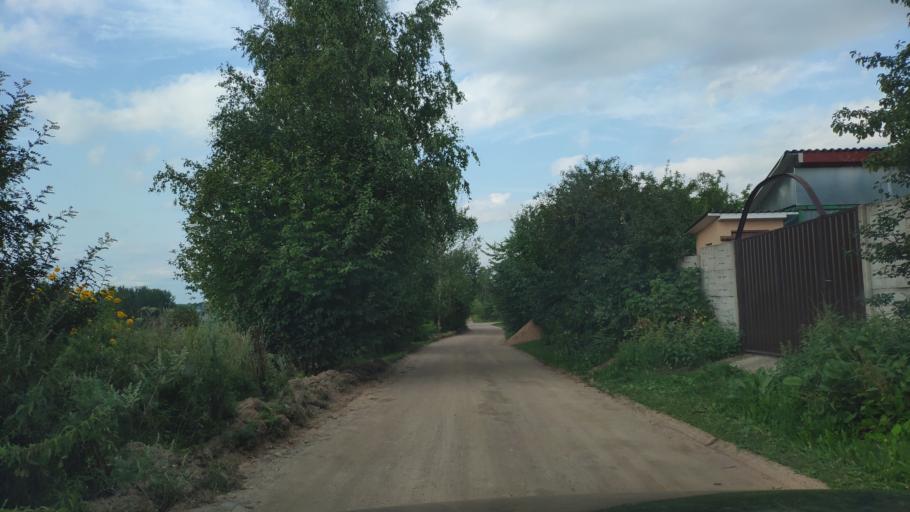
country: BY
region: Minsk
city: Khatsyezhyna
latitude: 53.8522
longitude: 27.2917
